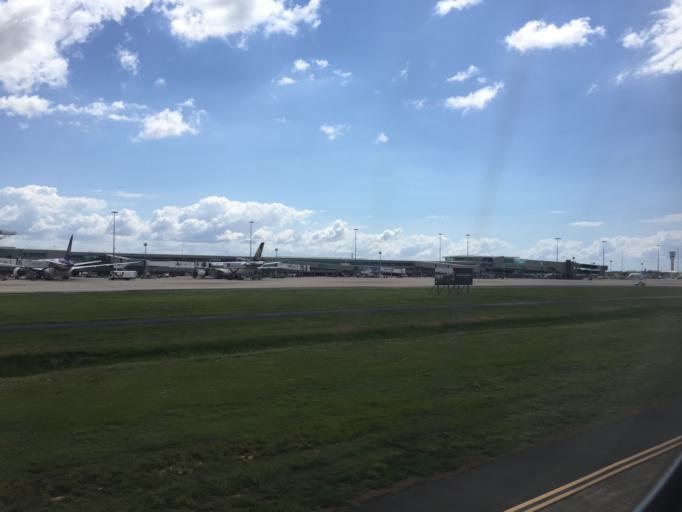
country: AU
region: Queensland
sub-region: Brisbane
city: Wynnum
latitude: -27.4050
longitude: 153.1133
